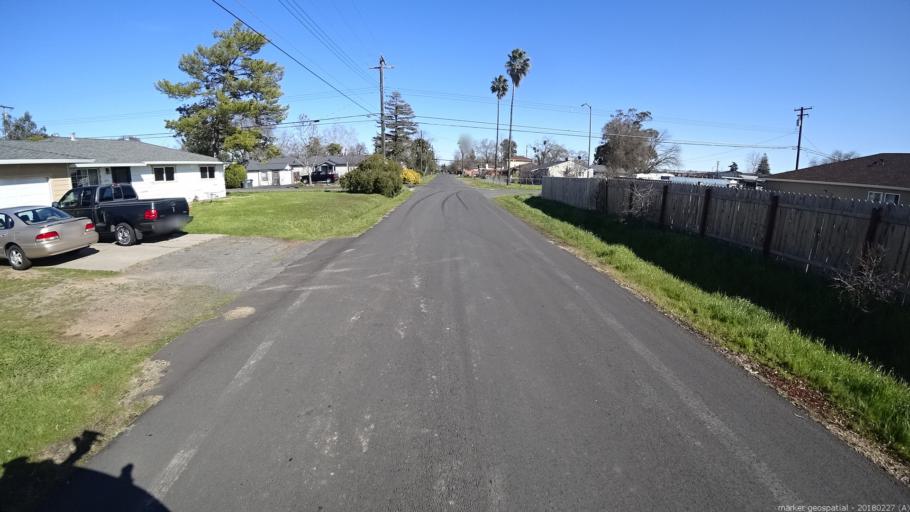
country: US
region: California
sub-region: Sacramento County
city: Rio Linda
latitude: 38.6929
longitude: -121.4493
